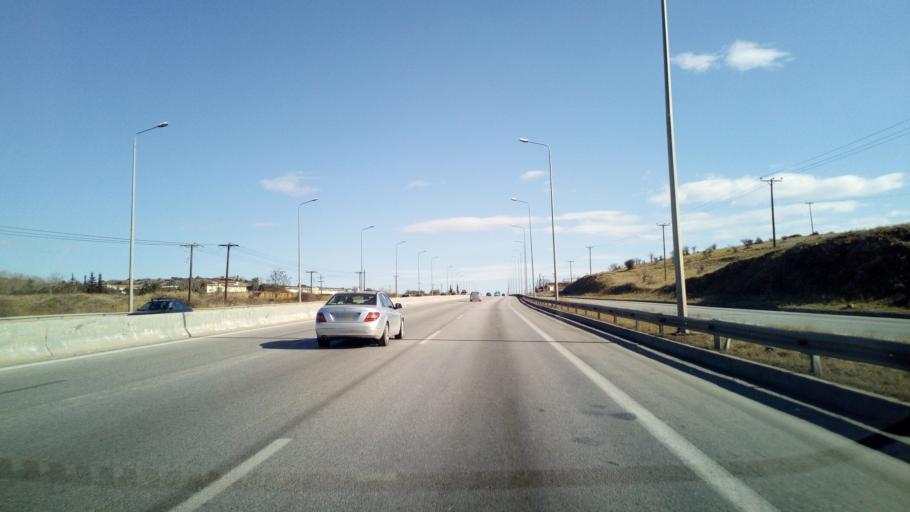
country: GR
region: Central Macedonia
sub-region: Nomos Thessalonikis
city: Efkarpia
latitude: 40.7170
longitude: 22.9656
